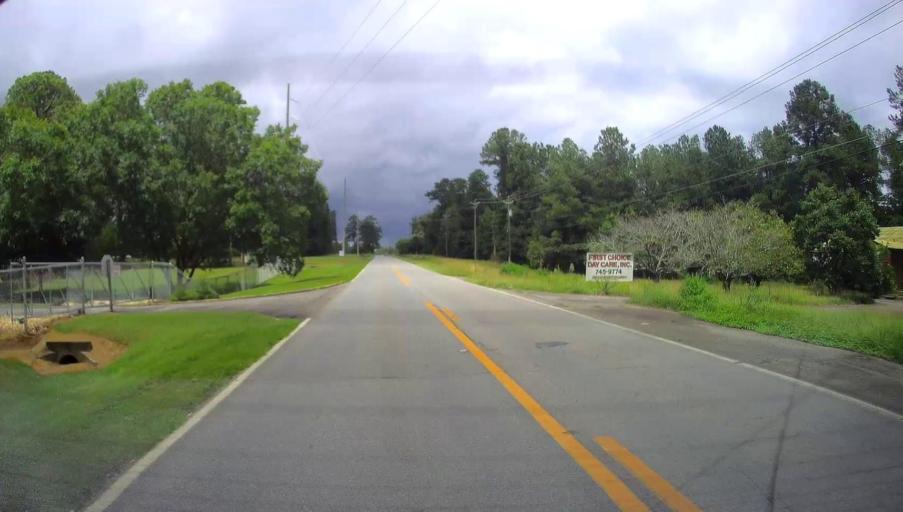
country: US
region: Georgia
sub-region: Bibb County
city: Macon
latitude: 32.8080
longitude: -83.5390
